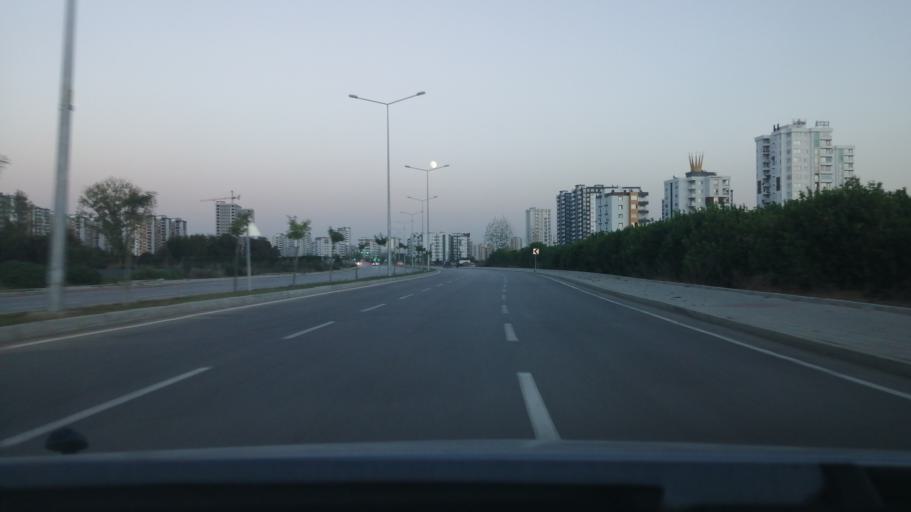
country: TR
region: Adana
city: Seyhan
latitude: 37.0153
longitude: 35.2525
